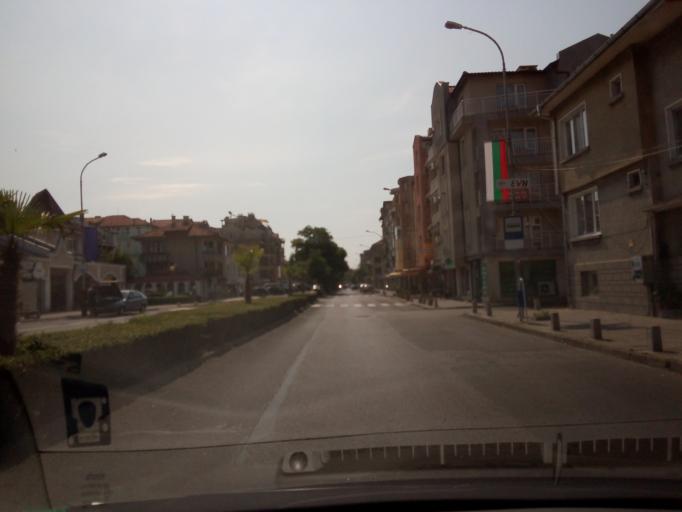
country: BG
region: Burgas
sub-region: Obshtina Pomorie
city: Pomorie
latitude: 42.5609
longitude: 27.6347
